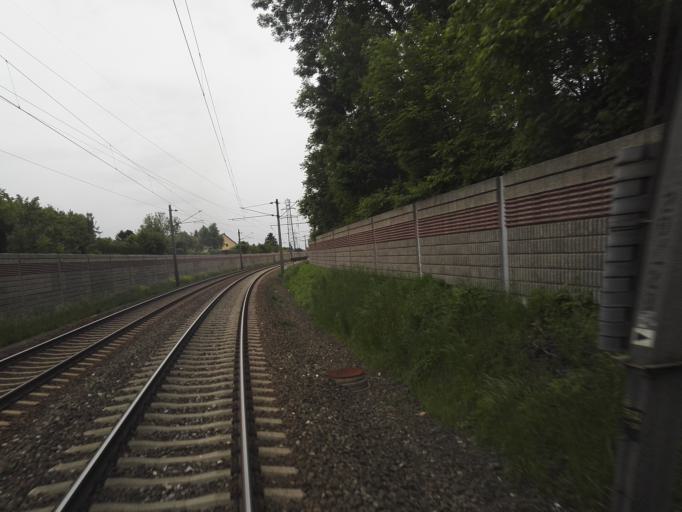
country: AT
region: Styria
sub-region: Graz Stadt
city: Goesting
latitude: 47.1046
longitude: 15.3961
